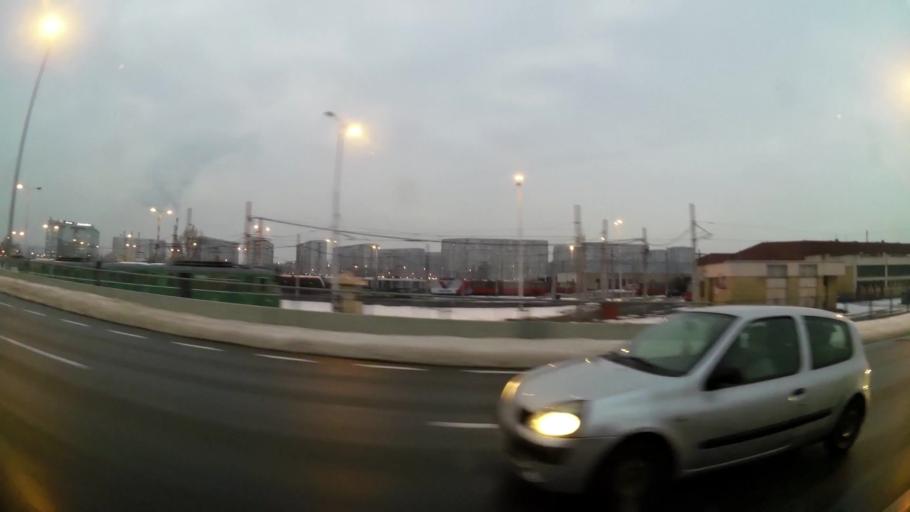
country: RS
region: Central Serbia
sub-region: Belgrade
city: Novi Beograd
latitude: 44.8093
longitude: 20.4110
